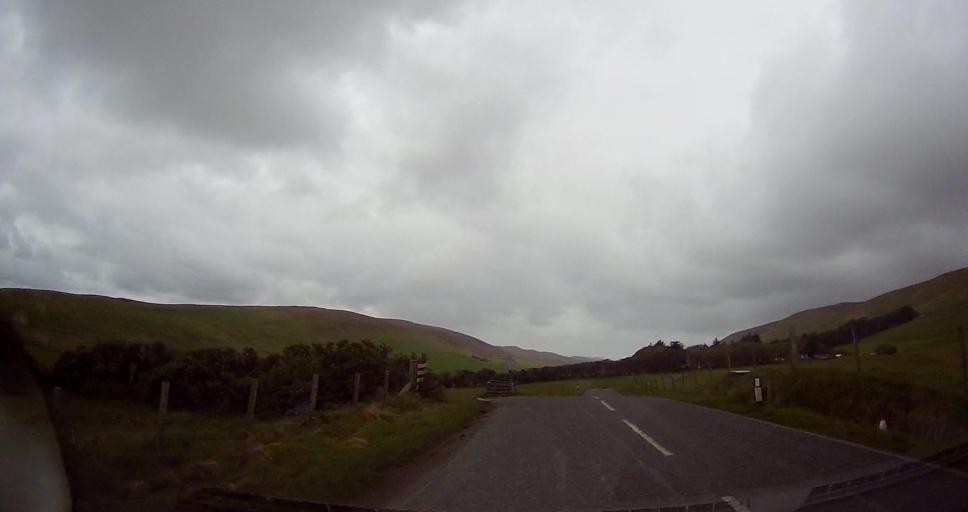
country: GB
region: Scotland
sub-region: Shetland Islands
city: Lerwick
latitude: 60.2747
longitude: -1.2843
